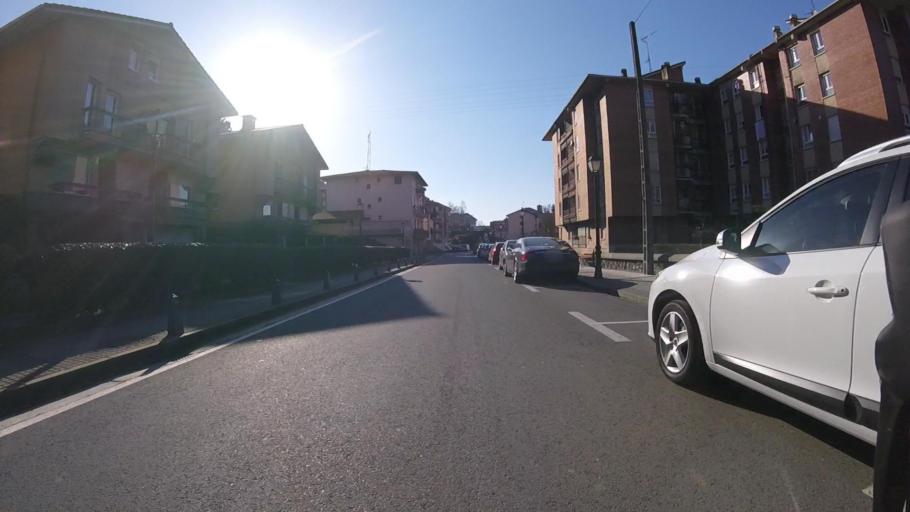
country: ES
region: Basque Country
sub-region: Provincia de Guipuzcoa
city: Astigarraga
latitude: 43.2819
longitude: -1.9439
